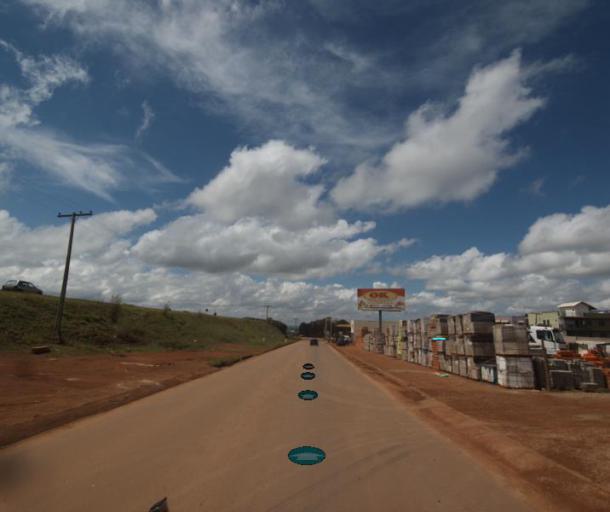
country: BR
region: Federal District
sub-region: Brasilia
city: Brasilia
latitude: -15.7541
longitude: -48.2584
